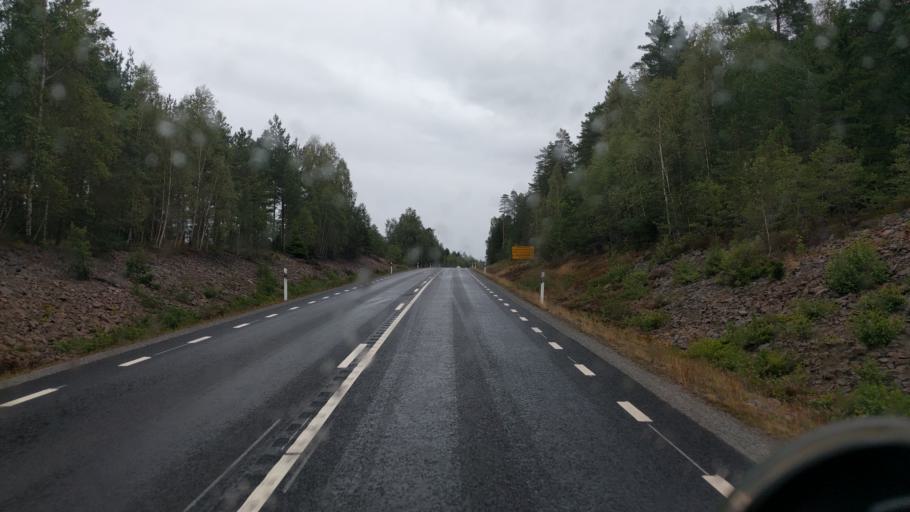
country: SE
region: Kalmar
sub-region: Vasterviks Kommun
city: Ankarsrum
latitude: 57.7133
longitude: 16.3386
